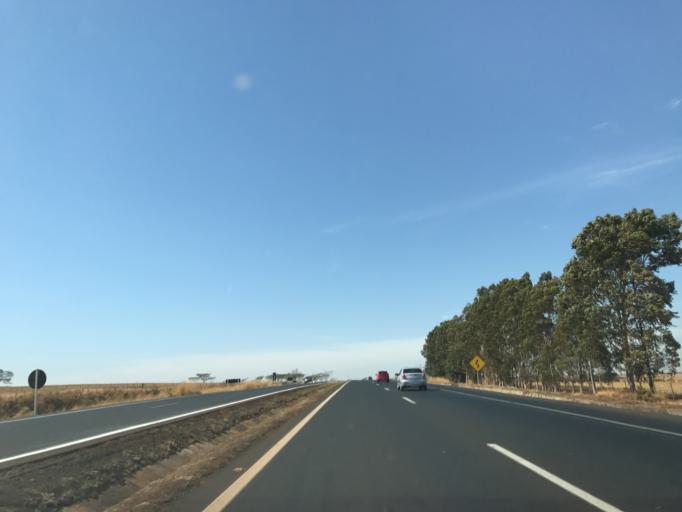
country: BR
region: Minas Gerais
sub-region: Centralina
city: Centralina
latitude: -18.6365
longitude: -49.1808
